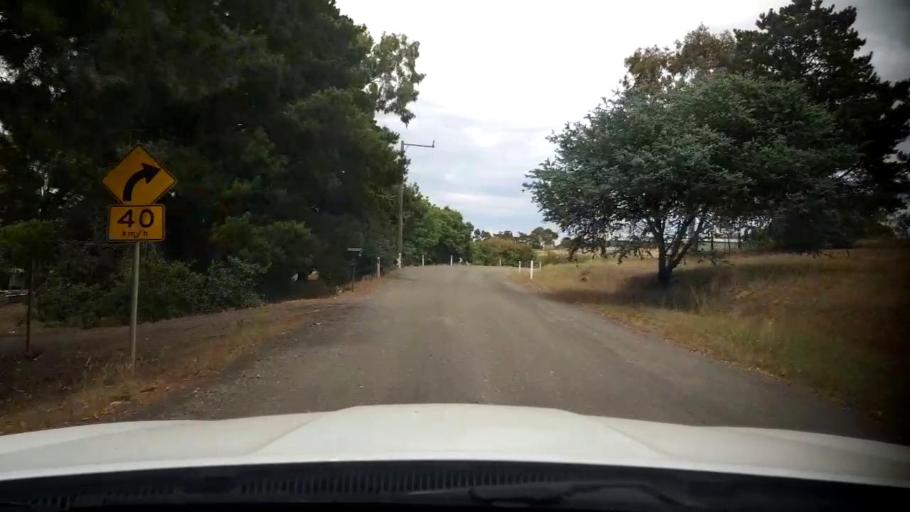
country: AU
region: Victoria
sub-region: Whittlesea
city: Whittlesea
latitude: -37.4896
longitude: 145.0639
